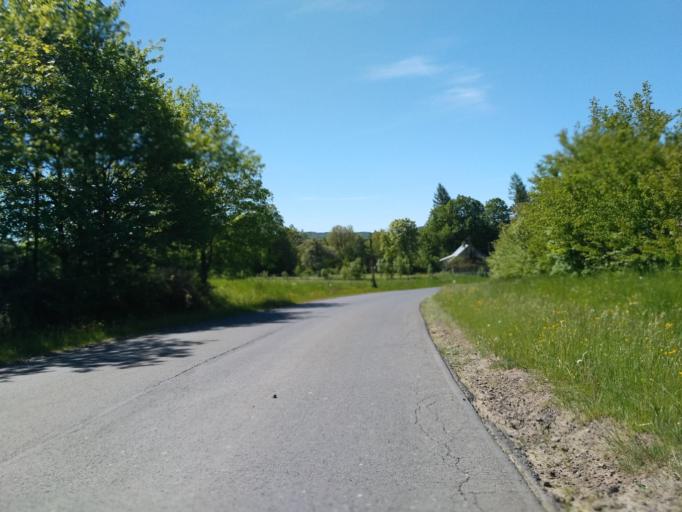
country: PL
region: Subcarpathian Voivodeship
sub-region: Powiat krosnienski
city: Sieniawa
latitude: 49.5624
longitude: 21.9396
